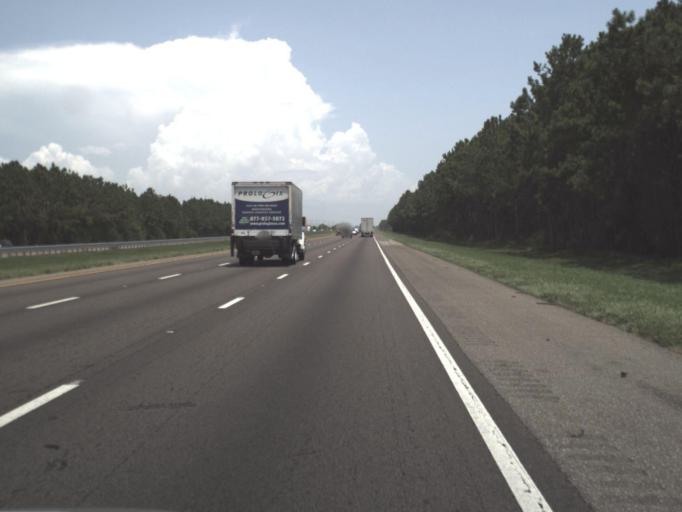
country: US
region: Florida
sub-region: Hillsborough County
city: Ruskin
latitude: 27.6584
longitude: -82.4367
